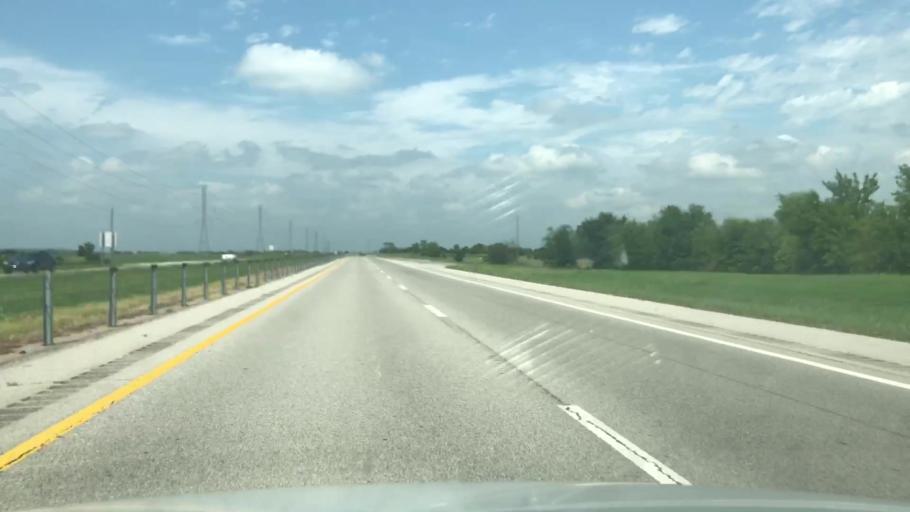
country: US
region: Oklahoma
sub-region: Tulsa County
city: Sperry
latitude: 36.3240
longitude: -95.9238
